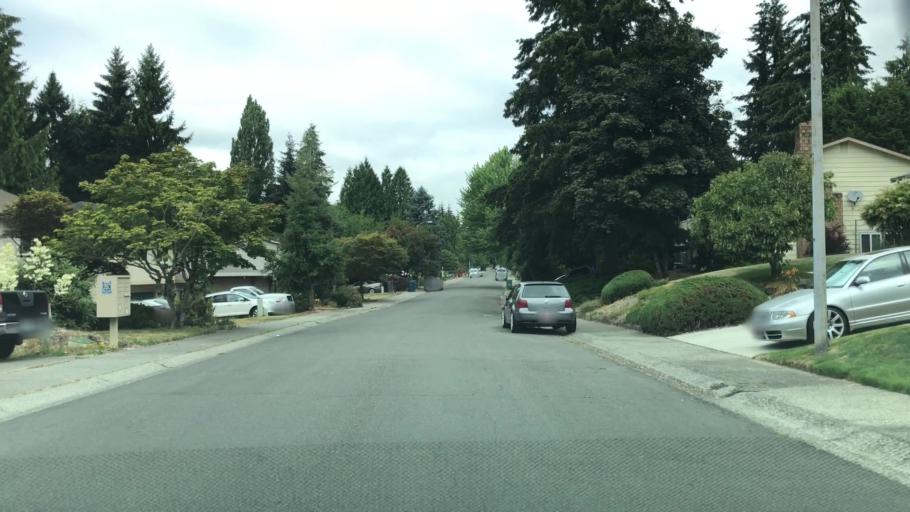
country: US
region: Washington
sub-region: King County
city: Kingsgate
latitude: 47.7208
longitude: -122.1872
